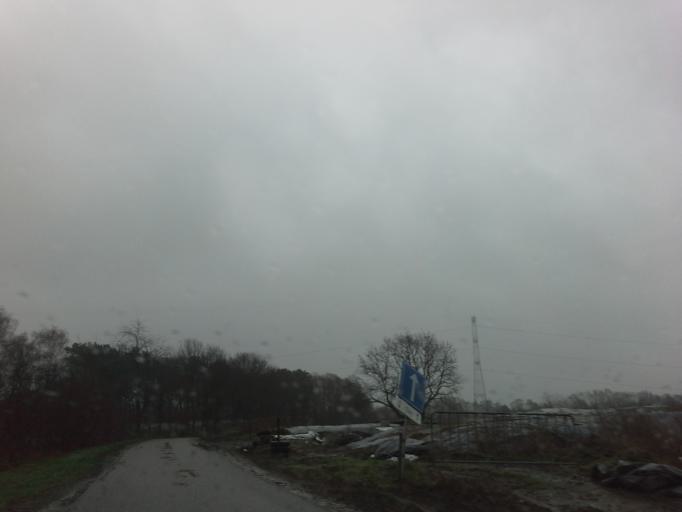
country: BE
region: Flanders
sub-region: Provincie Antwerpen
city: Meerhout
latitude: 51.1088
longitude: 5.1327
